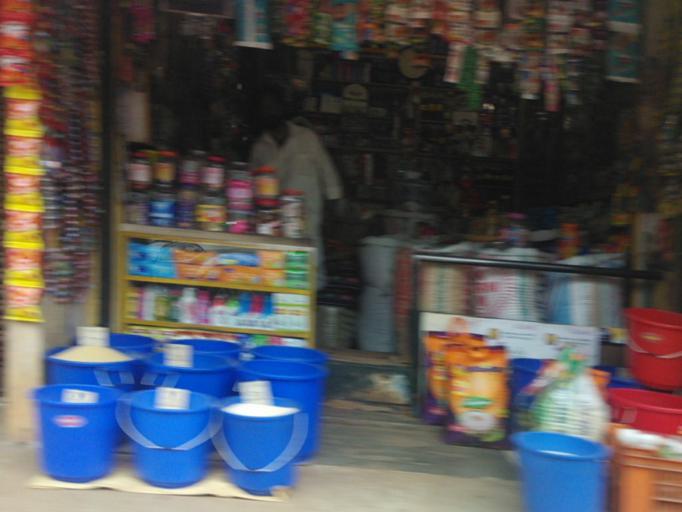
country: IN
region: Kerala
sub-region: Kozhikode
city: Kozhikode
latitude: 11.2893
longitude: 75.8121
